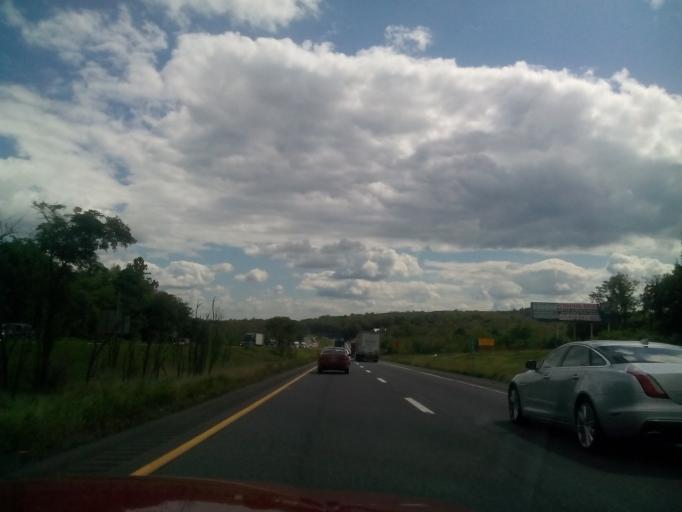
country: US
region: Pennsylvania
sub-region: Monroe County
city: Tannersville
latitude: 41.0378
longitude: -75.3122
